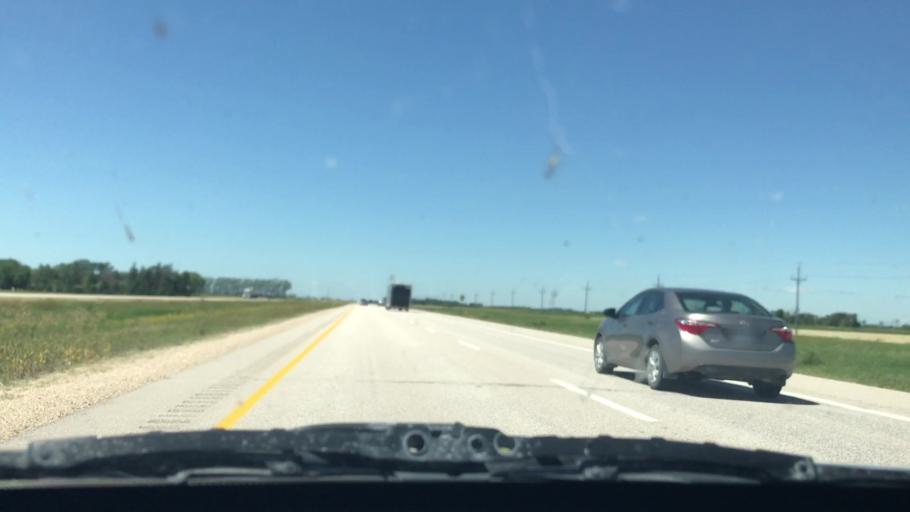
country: CA
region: Manitoba
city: Steinbach
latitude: 49.7305
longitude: -96.7193
